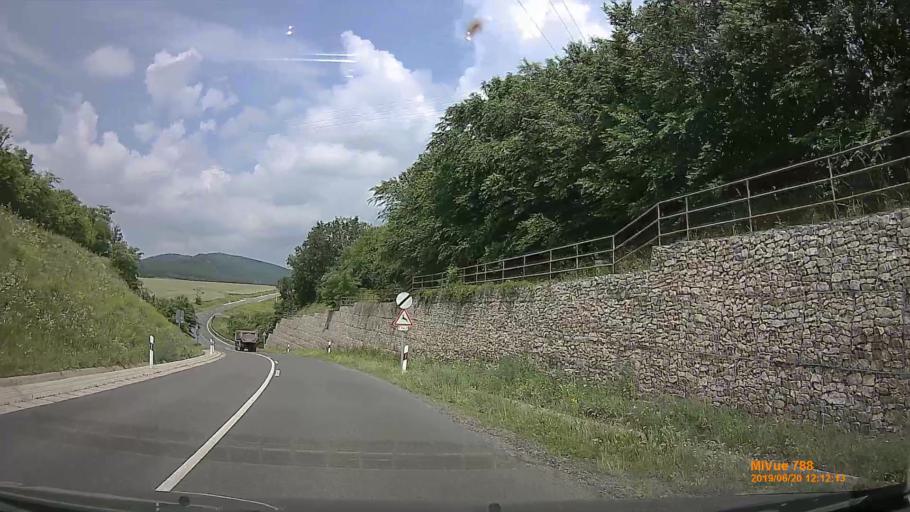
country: HU
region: Baranya
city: Hosszuheteny
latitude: 46.1449
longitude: 18.3487
